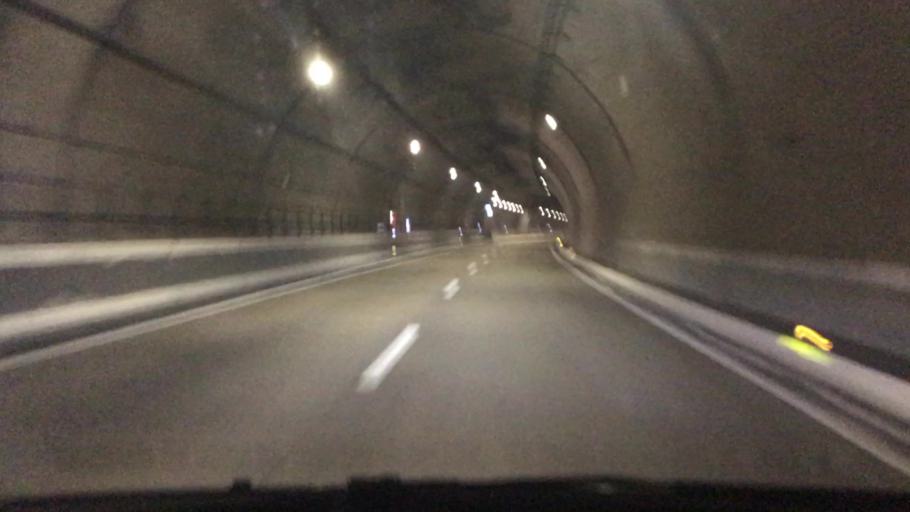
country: JP
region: Hyogo
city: Sandacho
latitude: 34.8048
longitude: 135.2456
